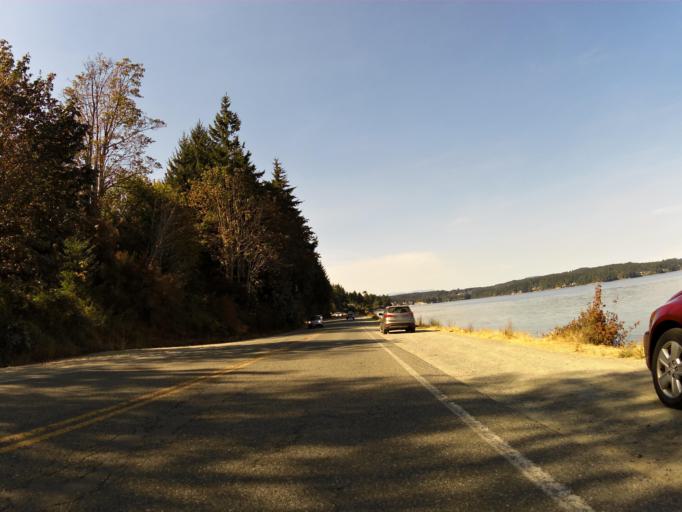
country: CA
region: British Columbia
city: North Saanich
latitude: 48.6335
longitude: -123.5322
